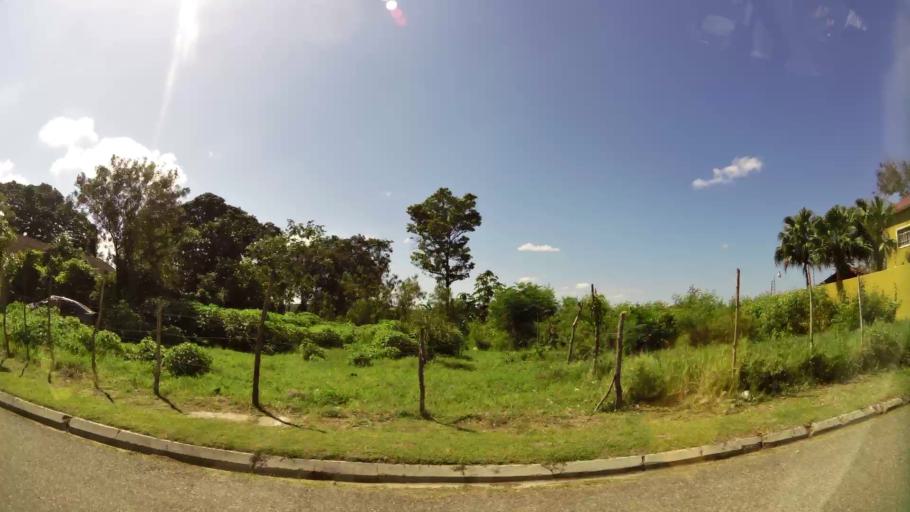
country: DO
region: San Cristobal
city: San Cristobal
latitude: 18.4337
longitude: -70.1274
